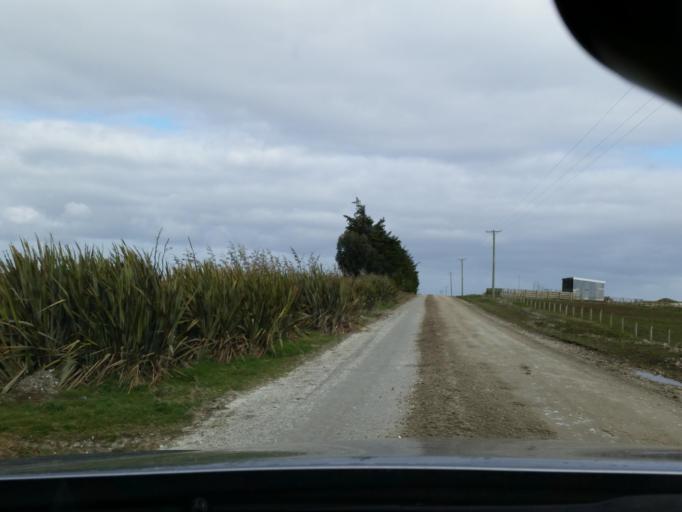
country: NZ
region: Southland
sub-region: Invercargill City
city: Invercargill
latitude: -46.4294
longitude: 168.5062
